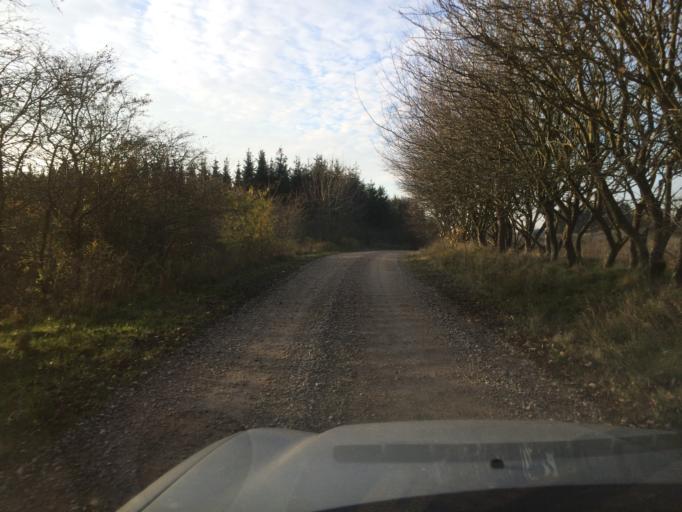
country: DK
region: Central Jutland
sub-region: Holstebro Kommune
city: Ulfborg
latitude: 56.2504
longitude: 8.4115
